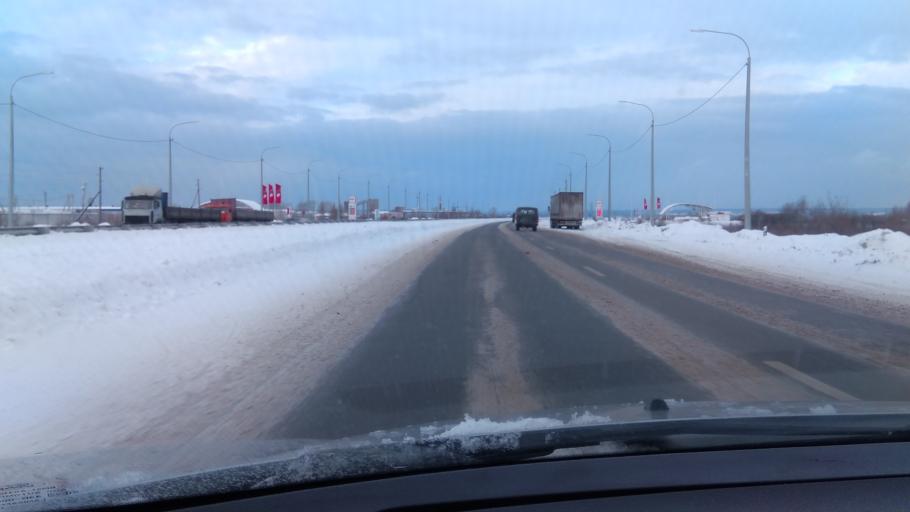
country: RU
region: Sverdlovsk
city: Tsementnyy
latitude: 57.4653
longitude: 60.1856
